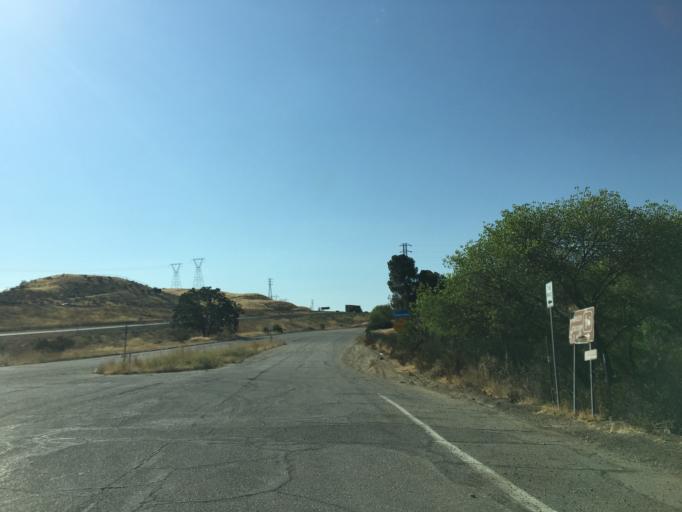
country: US
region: California
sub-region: Los Angeles County
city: Castaic
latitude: 34.5690
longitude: -118.6893
